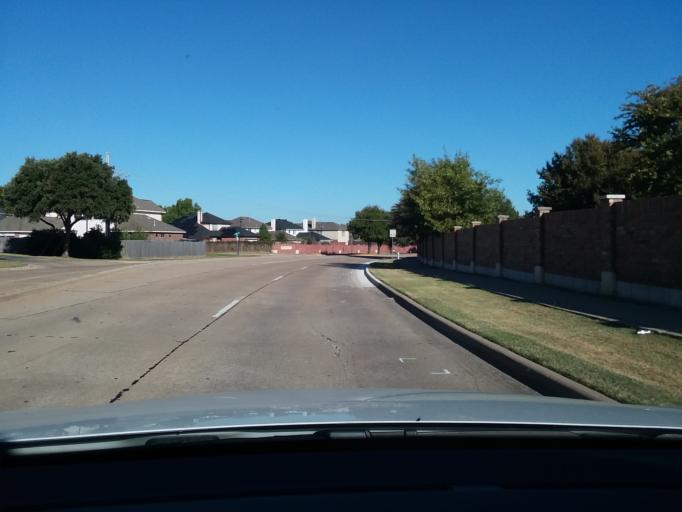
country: US
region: Texas
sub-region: Denton County
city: Lewisville
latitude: 33.0513
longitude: -97.0184
